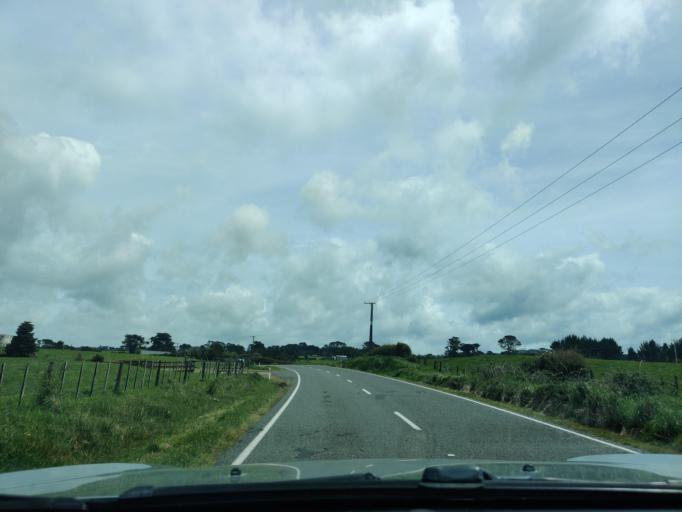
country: NZ
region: Taranaki
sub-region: South Taranaki District
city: Eltham
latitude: -39.3803
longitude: 174.1567
